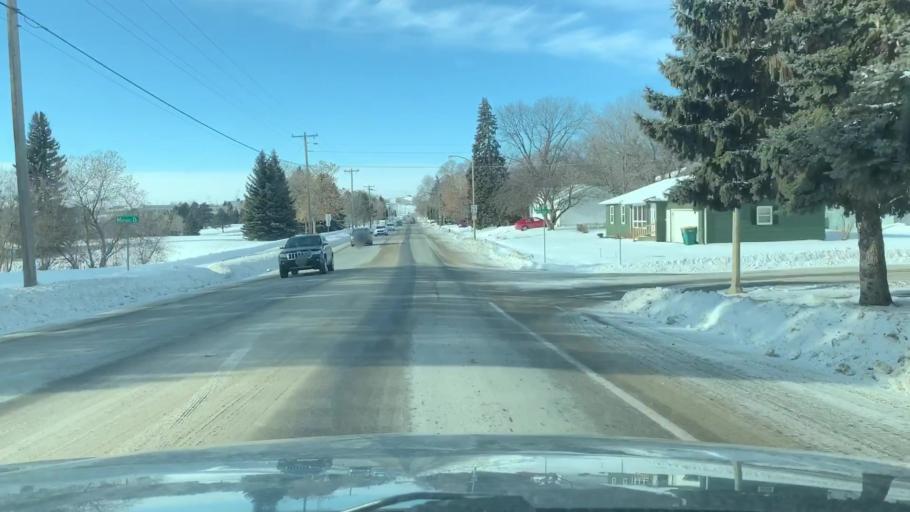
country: US
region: North Dakota
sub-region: Burleigh County
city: Bismarck
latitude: 46.8237
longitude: -100.7986
